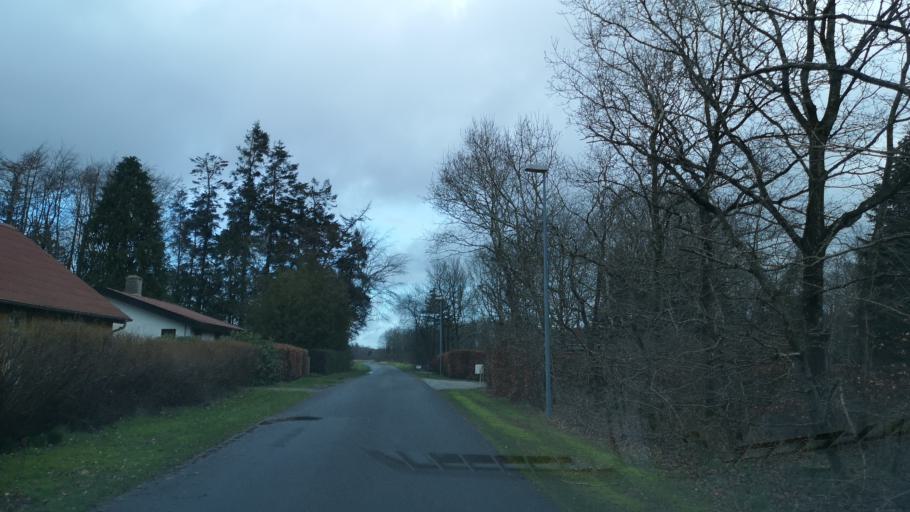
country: DK
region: Central Jutland
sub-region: Herning Kommune
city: Lind
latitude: 56.0047
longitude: 8.9700
